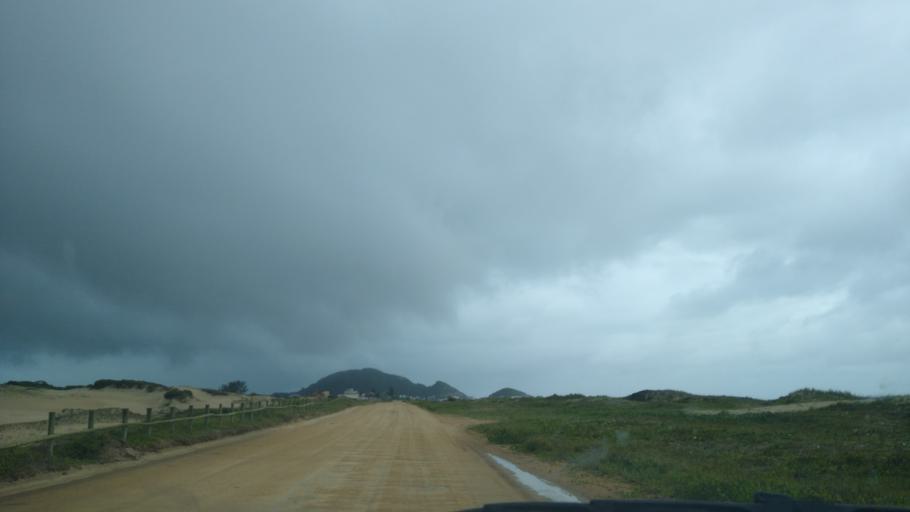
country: BR
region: Santa Catarina
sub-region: Sao Francisco Do Sul
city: Sao Francisco do Sul
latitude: -26.2449
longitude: -48.5096
